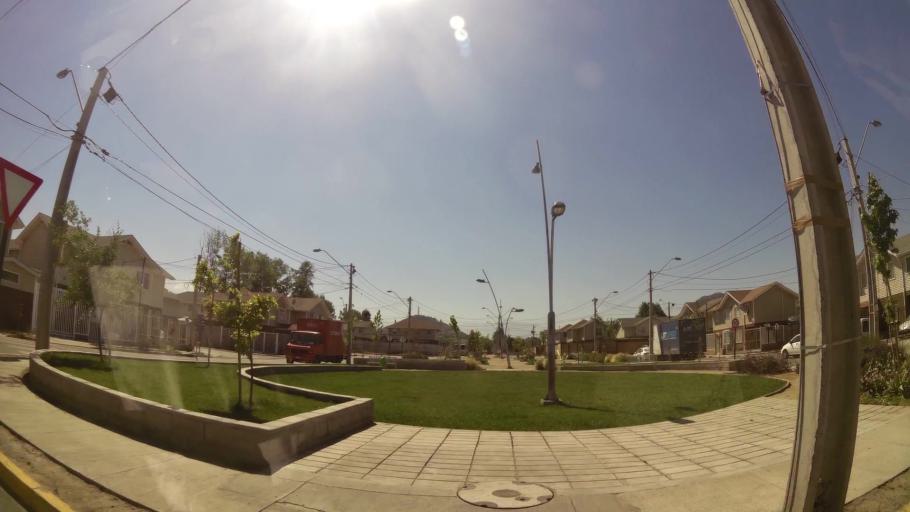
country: CL
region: Santiago Metropolitan
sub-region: Provincia de Maipo
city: San Bernardo
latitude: -33.6125
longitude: -70.6897
